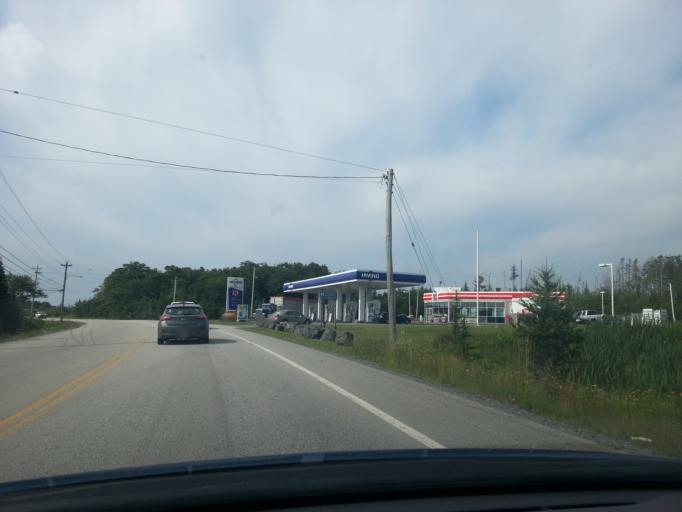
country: CA
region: Nova Scotia
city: Halifax
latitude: 44.6085
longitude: -63.6720
